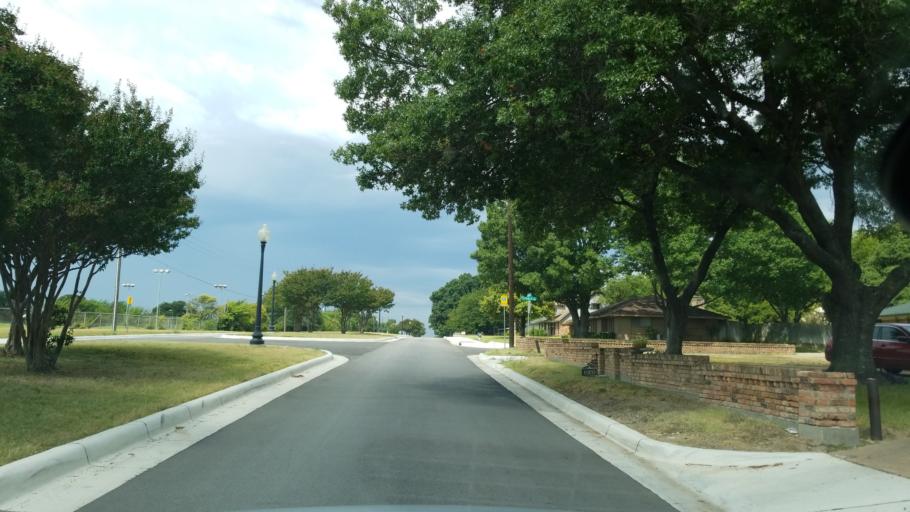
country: US
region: Texas
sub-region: Dallas County
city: Duncanville
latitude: 32.6718
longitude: -96.8508
